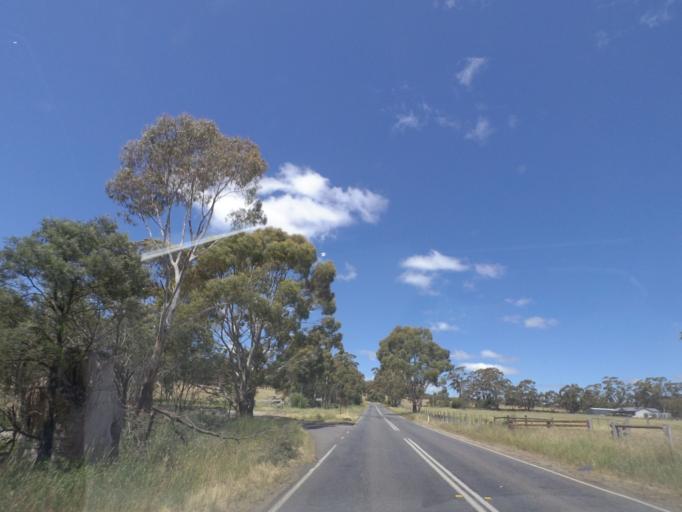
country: AU
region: Victoria
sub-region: Mount Alexander
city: Castlemaine
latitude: -37.2913
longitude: 144.2527
